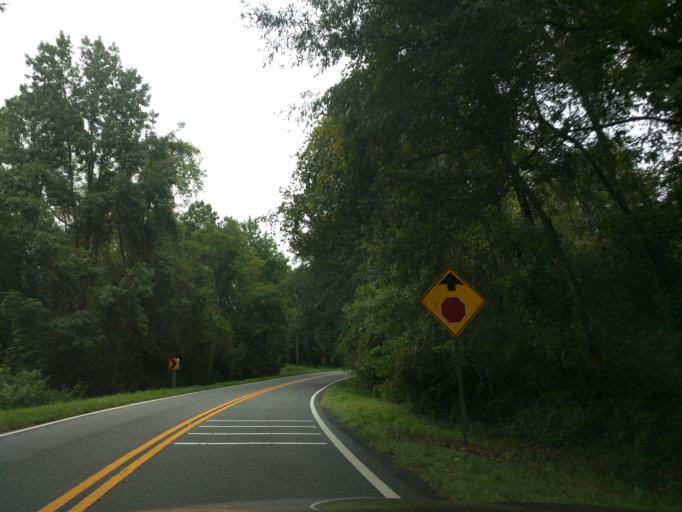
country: US
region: Florida
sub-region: Leon County
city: Tallahassee
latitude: 30.5148
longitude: -84.1291
